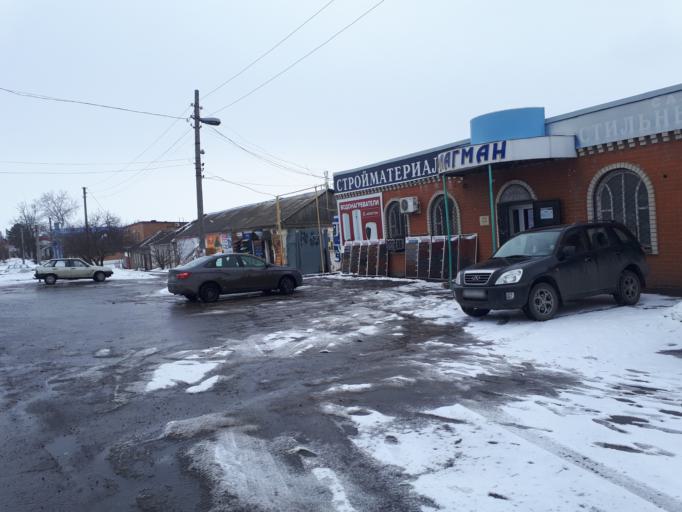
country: RU
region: Rostov
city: Krasnyy Sulin
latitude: 47.8990
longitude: 40.0553
